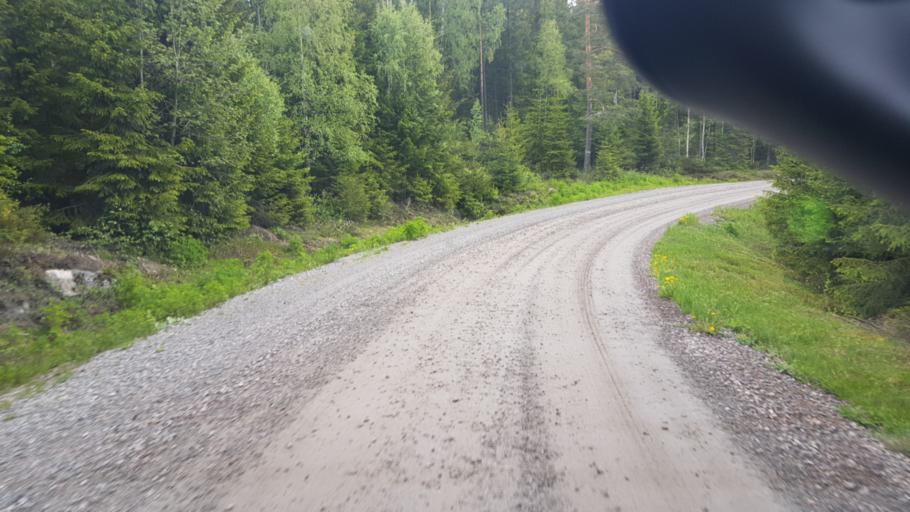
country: NO
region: Ostfold
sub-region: Romskog
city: Romskog
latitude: 59.7107
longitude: 12.0353
